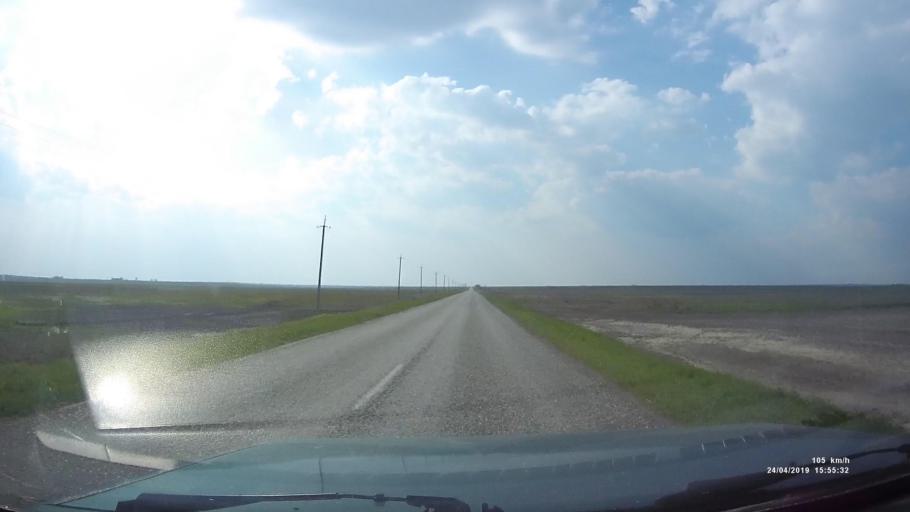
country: RU
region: Kalmykiya
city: Yashalta
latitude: 46.5912
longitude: 42.5472
